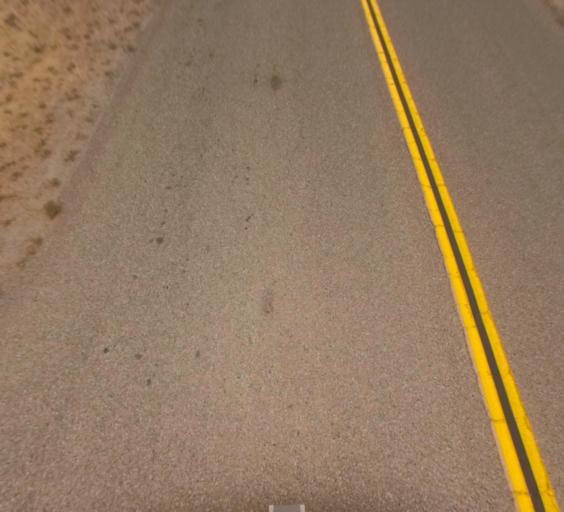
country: US
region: California
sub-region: Madera County
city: Coarsegold
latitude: 37.2177
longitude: -119.6773
